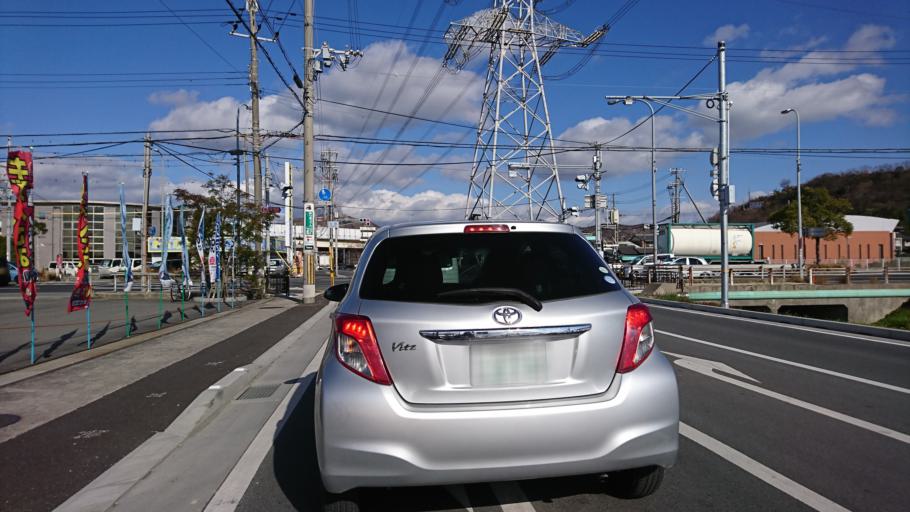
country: JP
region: Hyogo
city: Kakogawacho-honmachi
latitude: 34.7844
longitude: 134.7824
